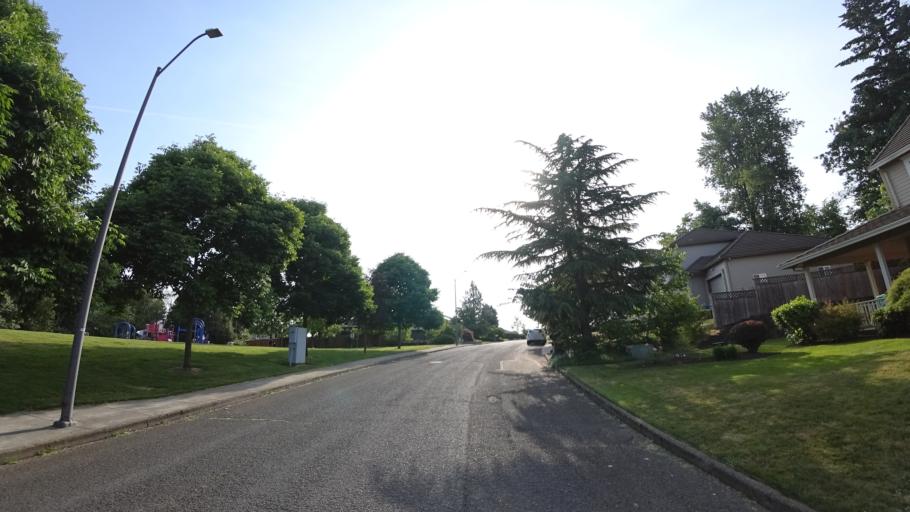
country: US
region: Oregon
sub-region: Clackamas County
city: Happy Valley
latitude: 45.4639
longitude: -122.5178
